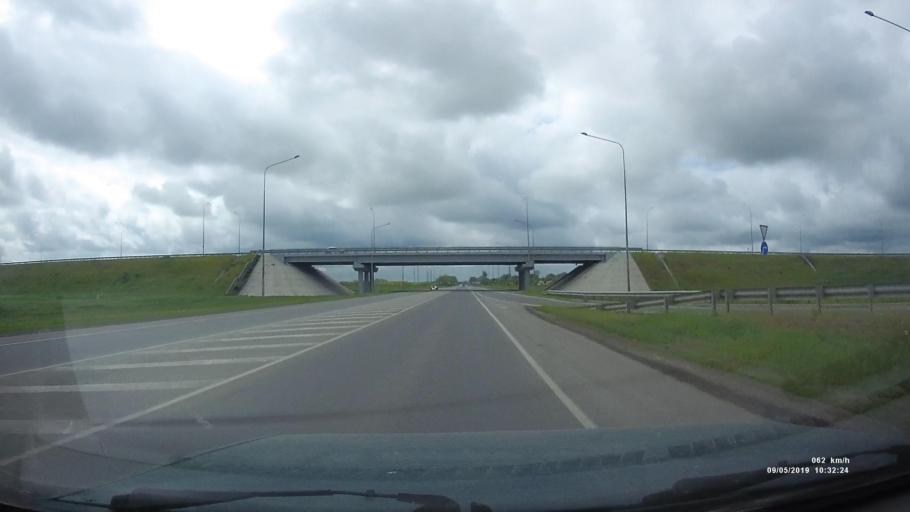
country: RU
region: Rostov
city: Azov
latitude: 47.0727
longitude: 39.4263
